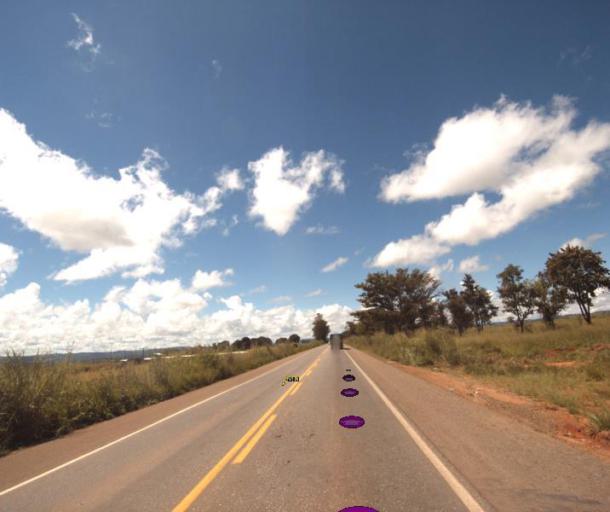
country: BR
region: Goias
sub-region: Pirenopolis
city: Pirenopolis
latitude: -16.0302
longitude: -49.0927
